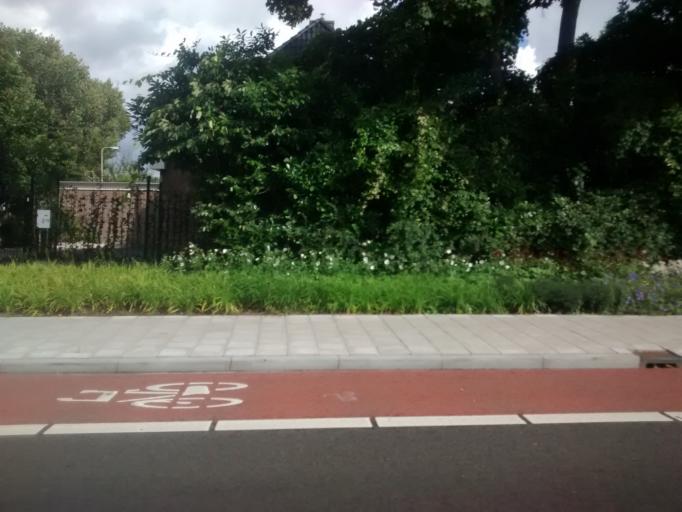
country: NL
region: Utrecht
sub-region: Gemeente Nieuwegein
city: Nieuwegein
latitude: 52.0386
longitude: 5.0893
